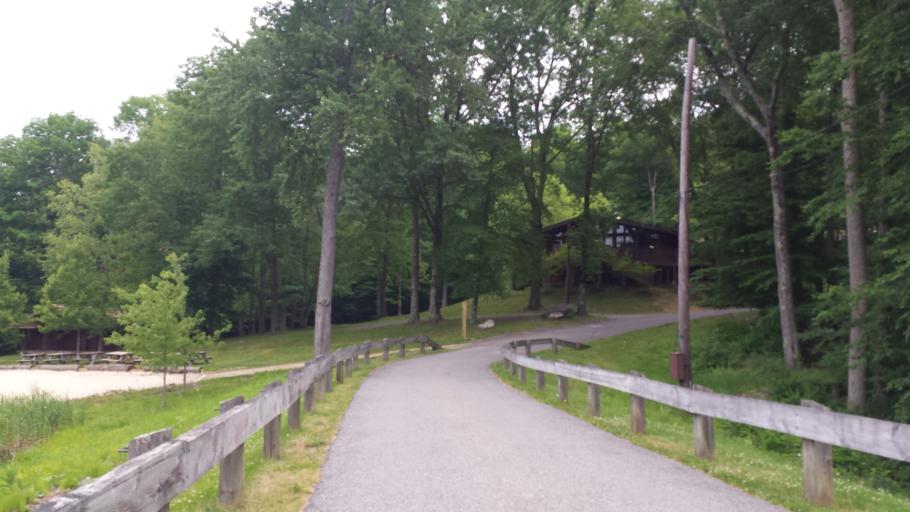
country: US
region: New York
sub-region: Putnam County
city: Peach Lake
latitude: 41.3092
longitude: -73.5697
